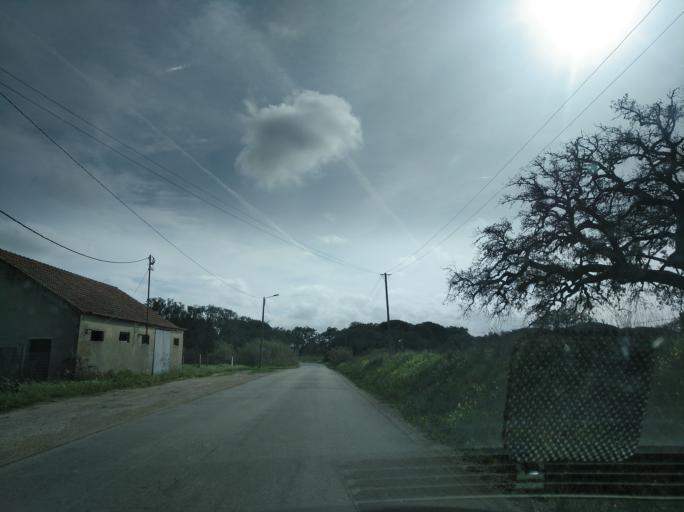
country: PT
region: Setubal
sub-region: Grandola
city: Grandola
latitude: 38.1875
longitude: -8.5563
